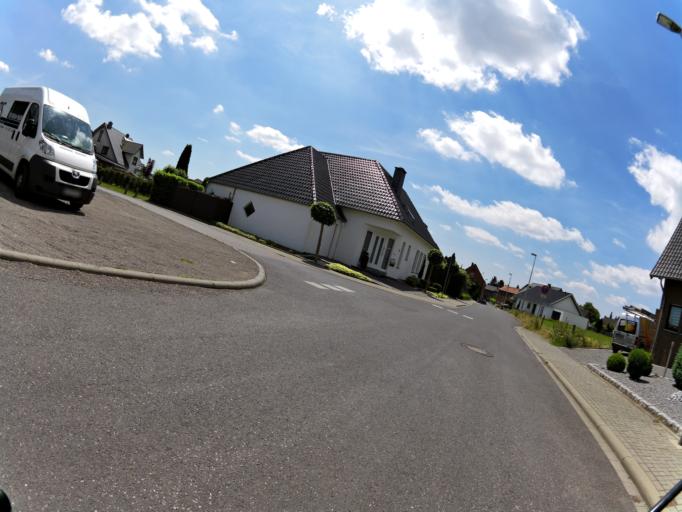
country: DE
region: North Rhine-Westphalia
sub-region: Regierungsbezirk Koln
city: Waldfeucht
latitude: 51.0300
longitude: 5.9914
